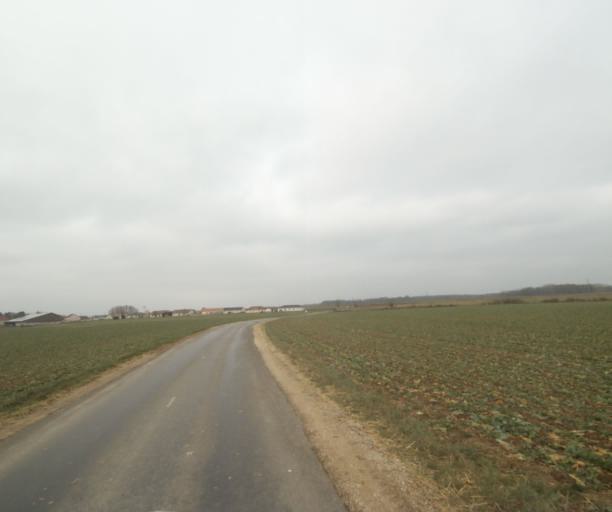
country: FR
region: Champagne-Ardenne
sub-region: Departement de la Haute-Marne
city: Villiers-en-Lieu
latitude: 48.6816
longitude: 4.8436
